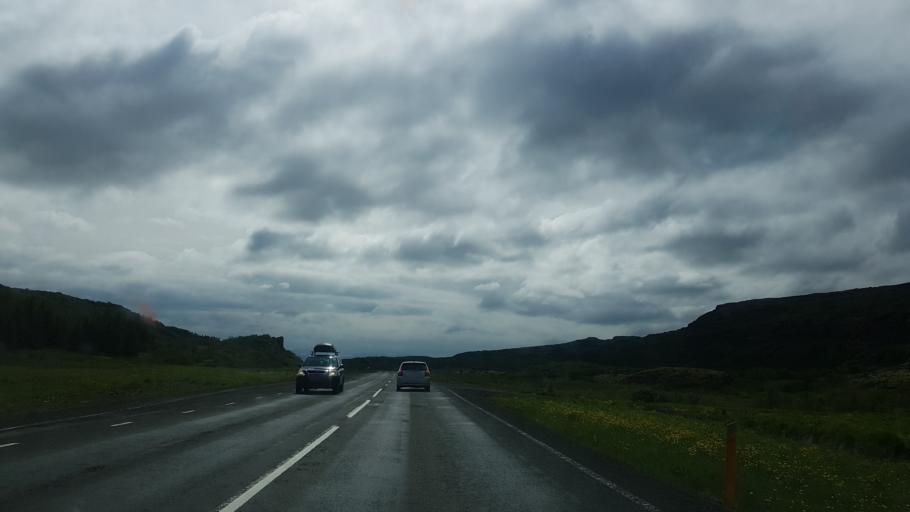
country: IS
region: West
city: Borgarnes
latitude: 64.7352
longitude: -21.5908
